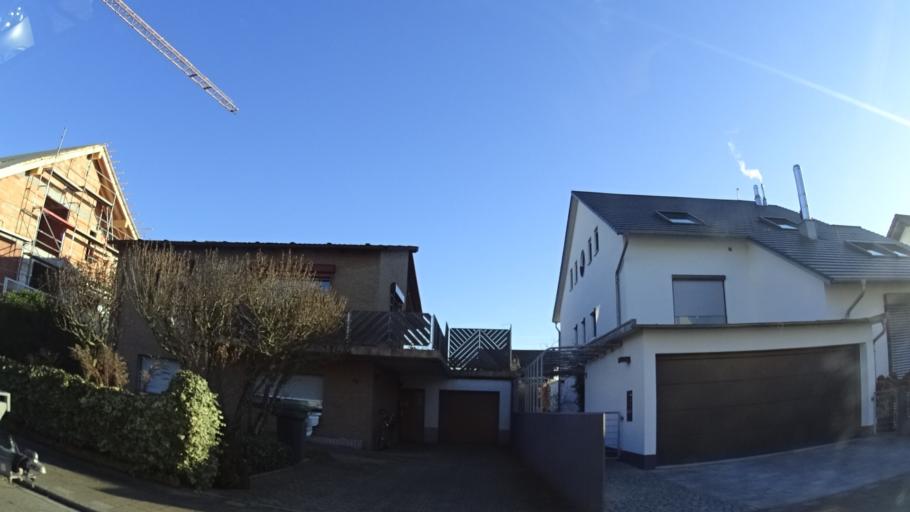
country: DE
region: Baden-Wuerttemberg
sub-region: Karlsruhe Region
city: Sankt Leon-Rot
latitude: 49.2638
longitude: 8.6223
